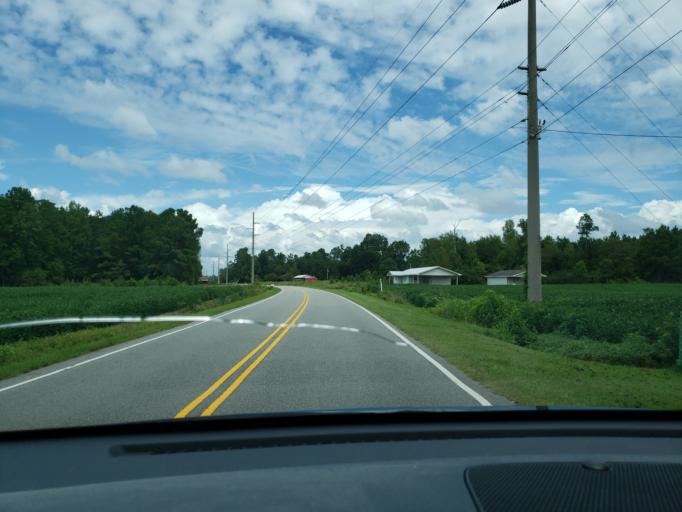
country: US
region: North Carolina
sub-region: Columbus County
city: Tabor City
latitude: 34.1650
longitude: -78.7821
